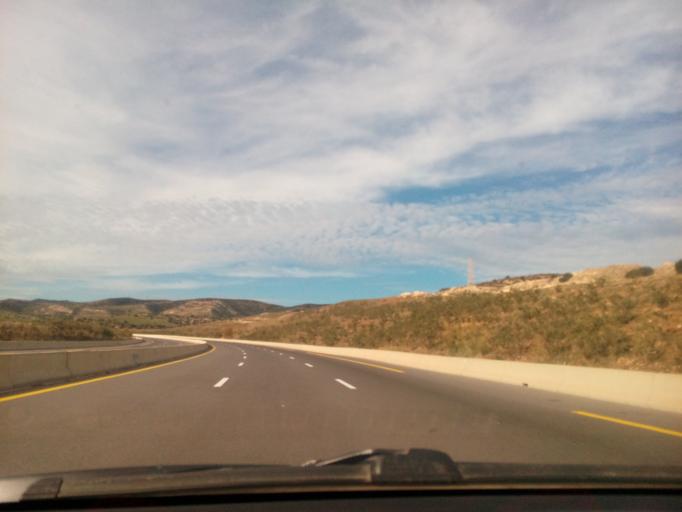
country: DZ
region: Sidi Bel Abbes
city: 'Ain el Berd
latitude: 35.4378
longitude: -0.4407
